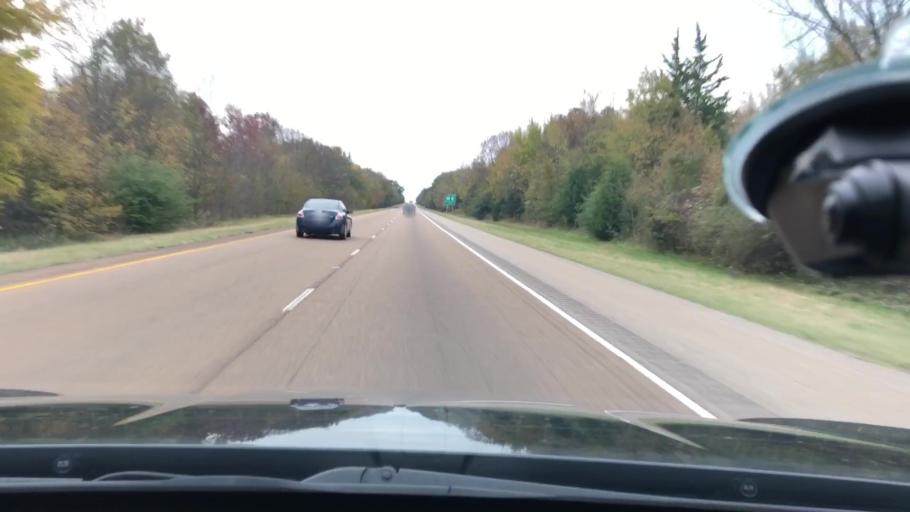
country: US
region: Arkansas
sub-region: Nevada County
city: Prescott
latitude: 33.7980
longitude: -93.4403
